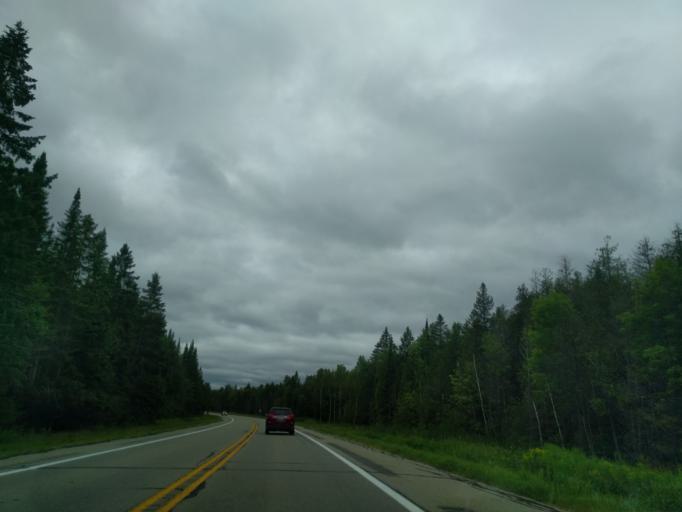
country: US
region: Michigan
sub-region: Delta County
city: Escanaba
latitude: 45.5937
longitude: -87.2347
